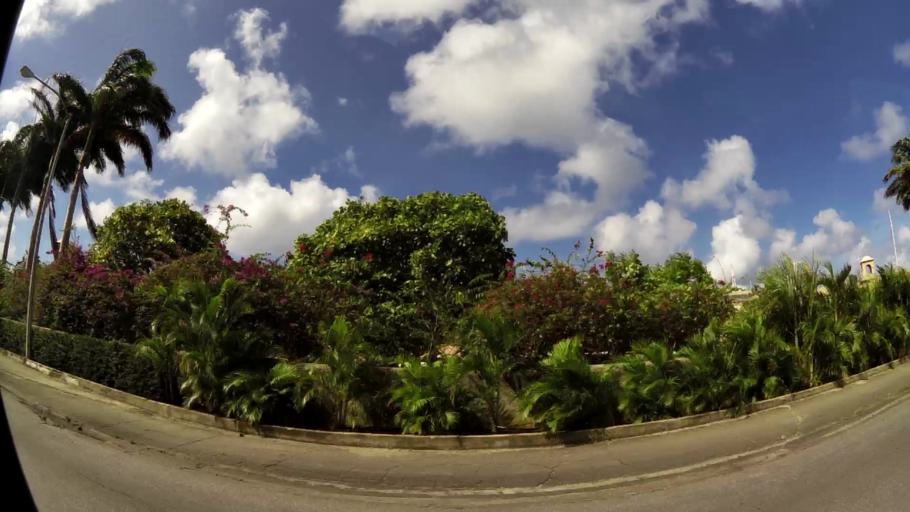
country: BB
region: Saint Peter
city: Speightstown
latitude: 13.2620
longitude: -59.6412
